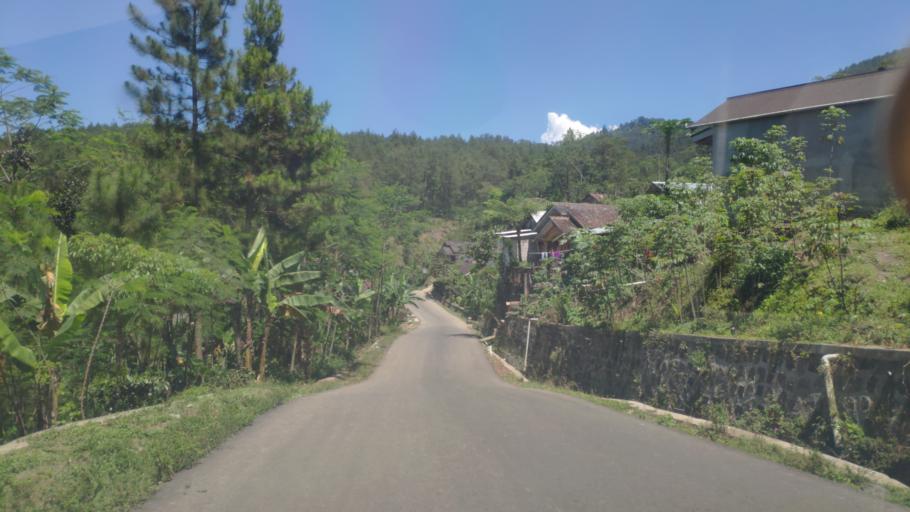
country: ID
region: Central Java
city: Buaran
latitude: -7.2422
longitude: 109.6564
